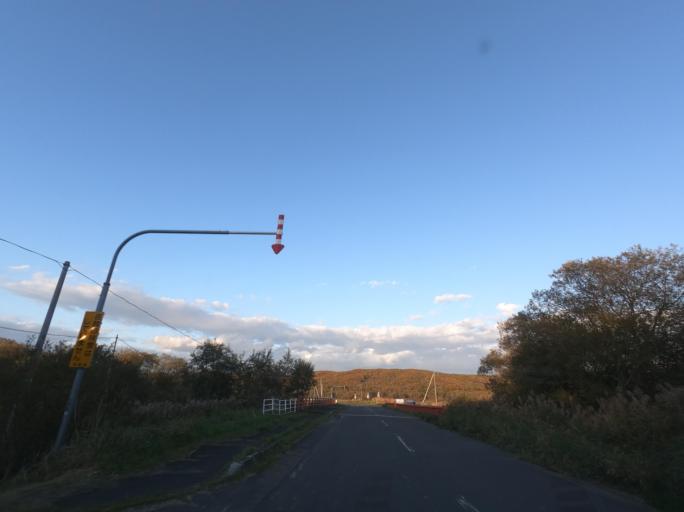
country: JP
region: Hokkaido
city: Kushiro
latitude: 43.2202
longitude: 144.4311
